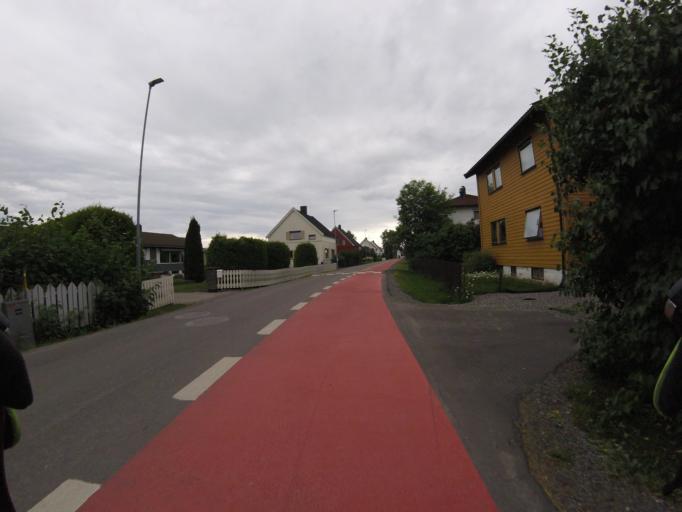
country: NO
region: Akershus
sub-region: Skedsmo
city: Lillestrom
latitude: 59.9624
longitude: 11.0359
